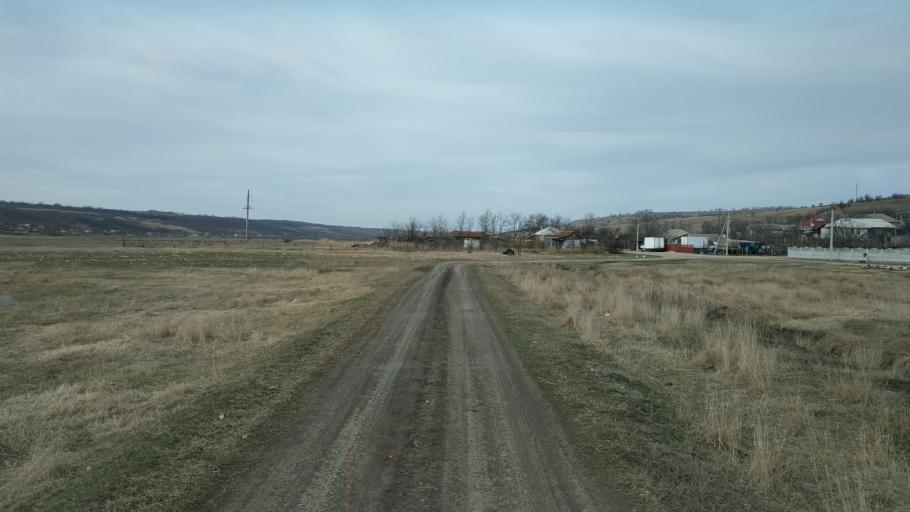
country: RO
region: Vaslui
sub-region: Comuna Dranceni
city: Dranceni
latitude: 46.8746
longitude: 28.2030
